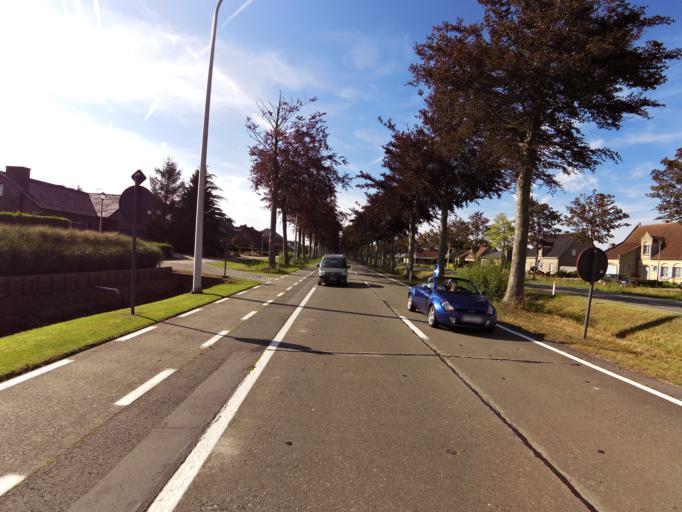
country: BE
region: Flanders
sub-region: Provincie Oost-Vlaanderen
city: Maldegem
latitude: 51.2168
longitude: 3.4146
